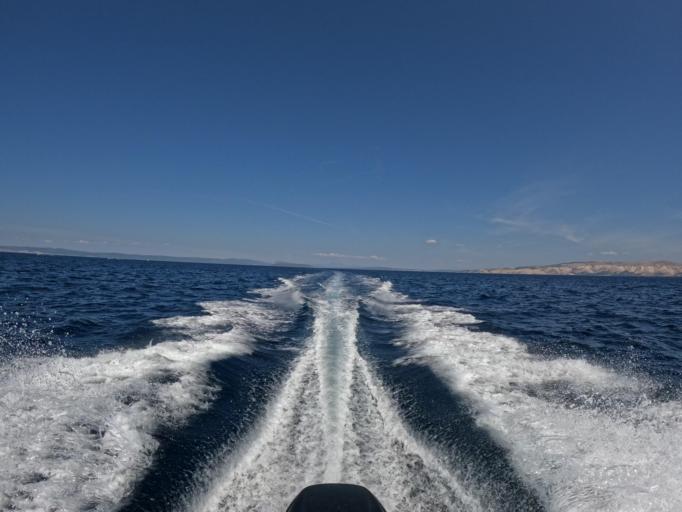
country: HR
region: Primorsko-Goranska
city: Lopar
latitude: 44.8796
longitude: 14.6586
